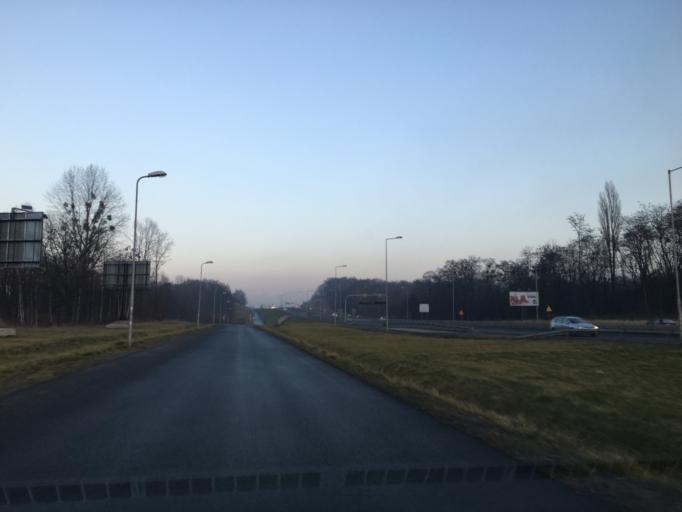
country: PL
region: Silesian Voivodeship
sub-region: Powiat tarnogorski
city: Radzionkow
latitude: 50.3504
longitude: 18.8533
